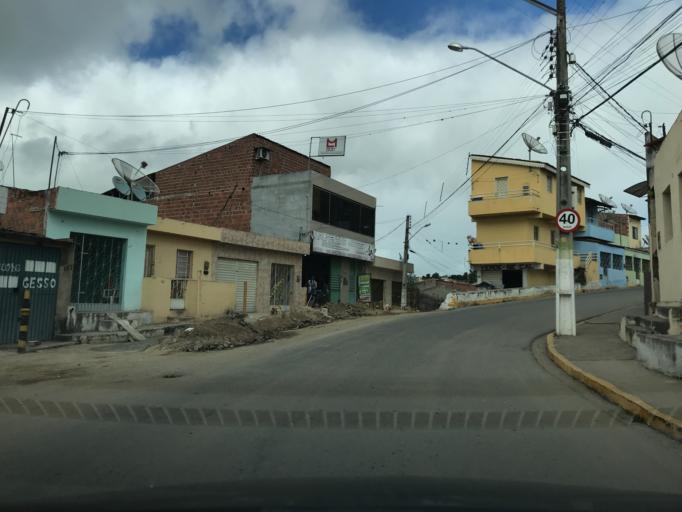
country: BR
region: Pernambuco
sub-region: Bezerros
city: Bezerros
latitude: -8.2306
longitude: -35.7514
